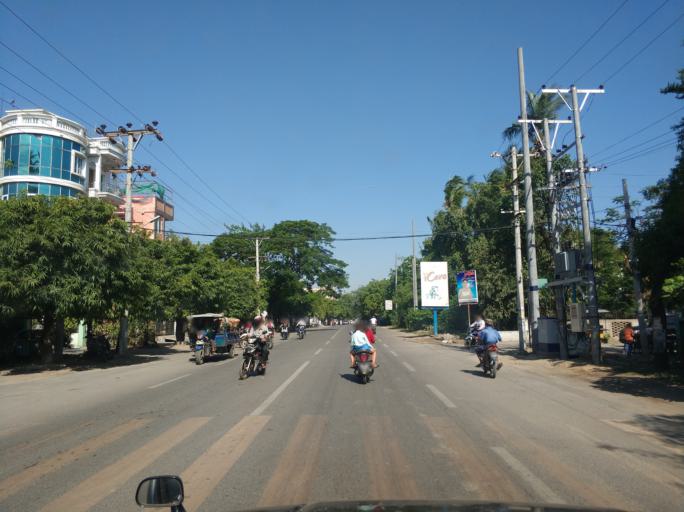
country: MM
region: Mandalay
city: Mandalay
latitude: 21.9706
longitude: 96.0654
